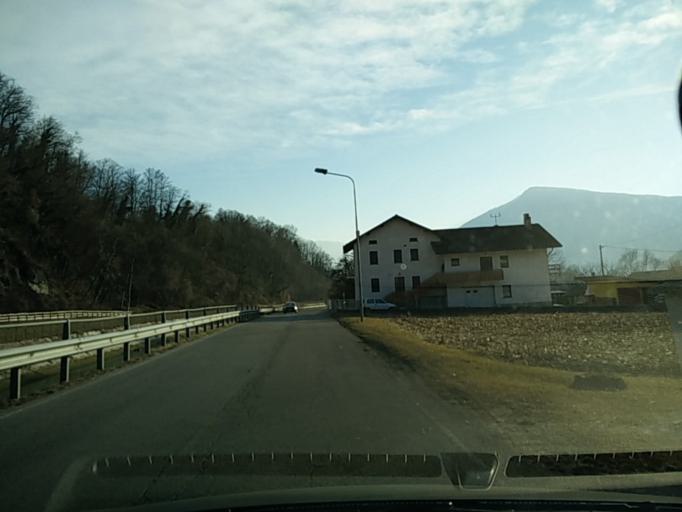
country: IT
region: Veneto
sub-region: Provincia di Belluno
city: Pieve d'Alpago
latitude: 46.1494
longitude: 12.3298
